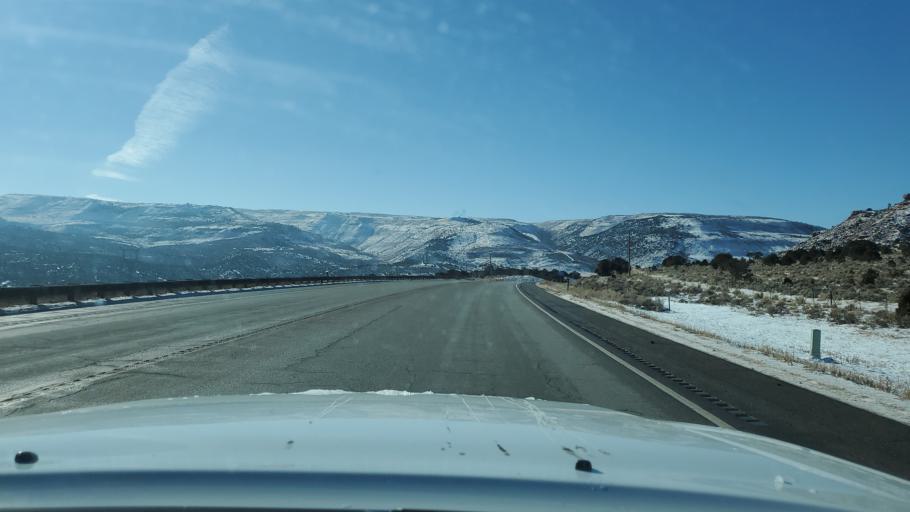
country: US
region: Utah
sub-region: Duchesne County
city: Duchesne
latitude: 40.2021
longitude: -110.8785
